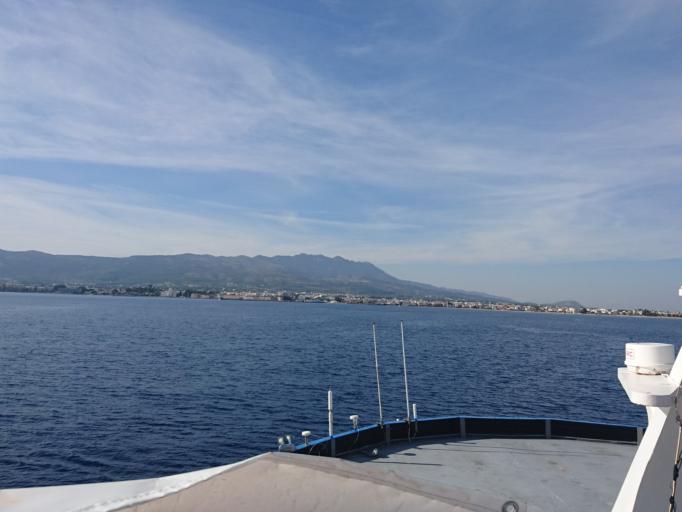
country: GR
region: South Aegean
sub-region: Nomos Dodekanisou
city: Kos
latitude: 36.9077
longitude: 27.2997
